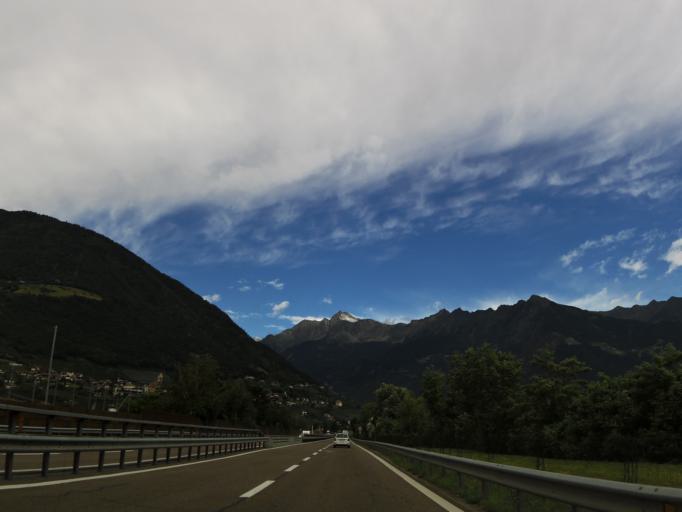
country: IT
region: Trentino-Alto Adige
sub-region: Bolzano
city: Marlengo
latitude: 46.6507
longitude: 11.1538
